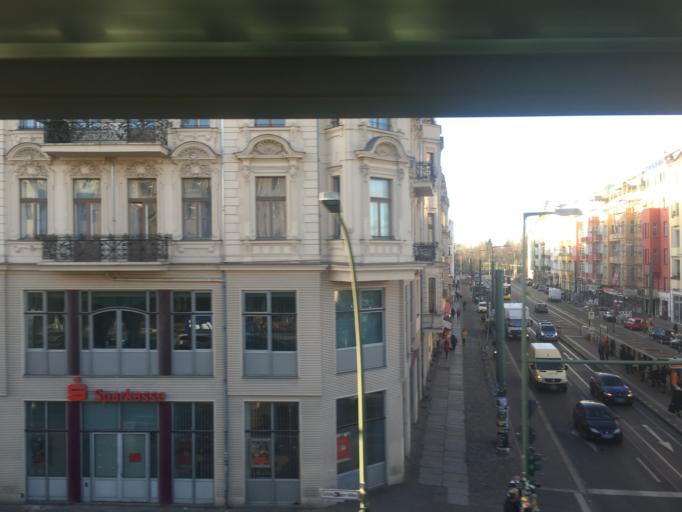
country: DE
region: Berlin
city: Prenzlauer Berg Bezirk
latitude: 52.5418
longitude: 13.4120
